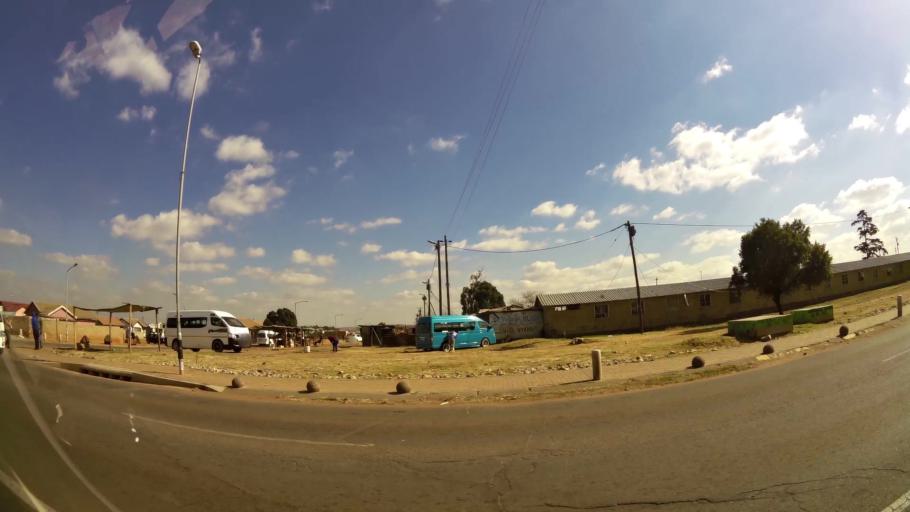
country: ZA
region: Gauteng
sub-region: West Rand District Municipality
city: Krugersdorp
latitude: -26.1433
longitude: 27.7921
